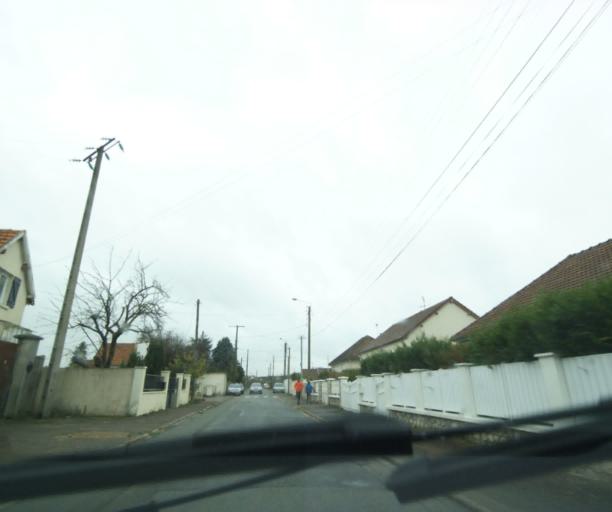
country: FR
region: Centre
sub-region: Departement d'Eure-et-Loir
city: Vernouillet
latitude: 48.7221
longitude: 1.3626
